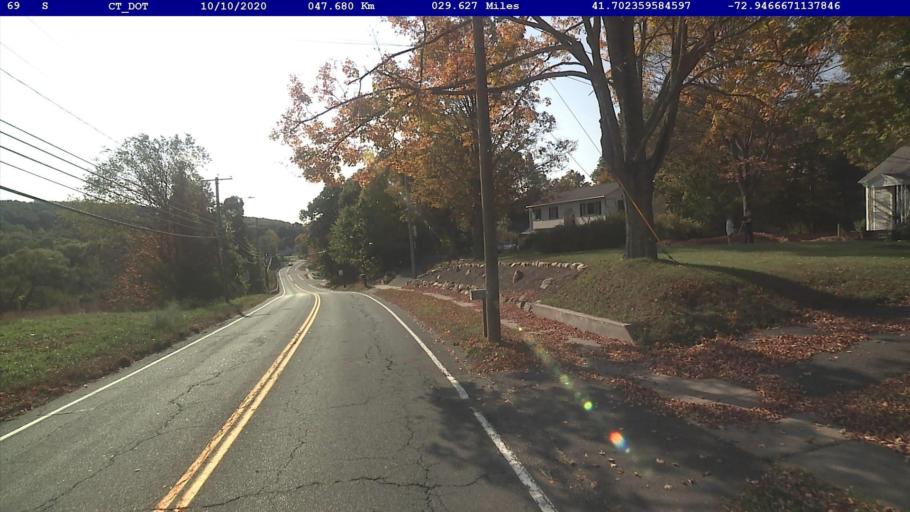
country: US
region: Connecticut
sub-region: Hartford County
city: Bristol
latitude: 41.7024
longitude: -72.9466
